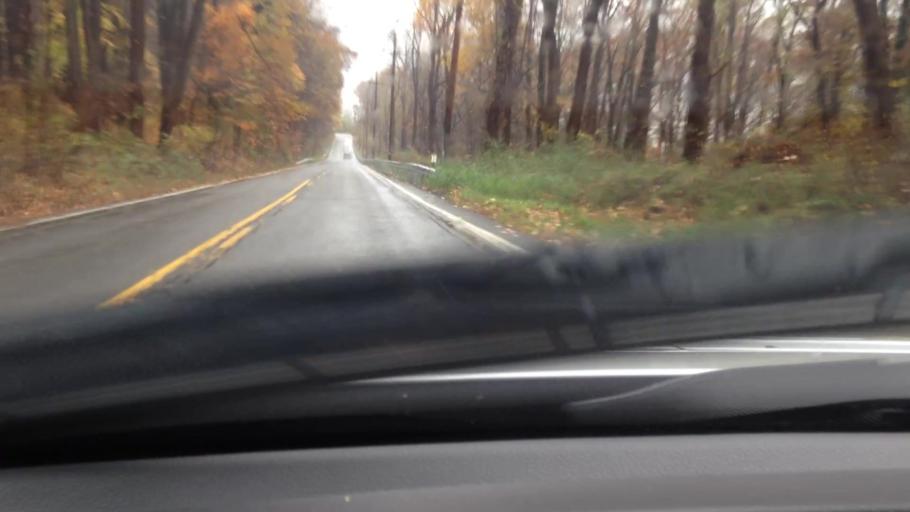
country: US
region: New York
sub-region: Orange County
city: Cornwall-on-Hudson
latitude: 41.4558
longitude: -73.9818
